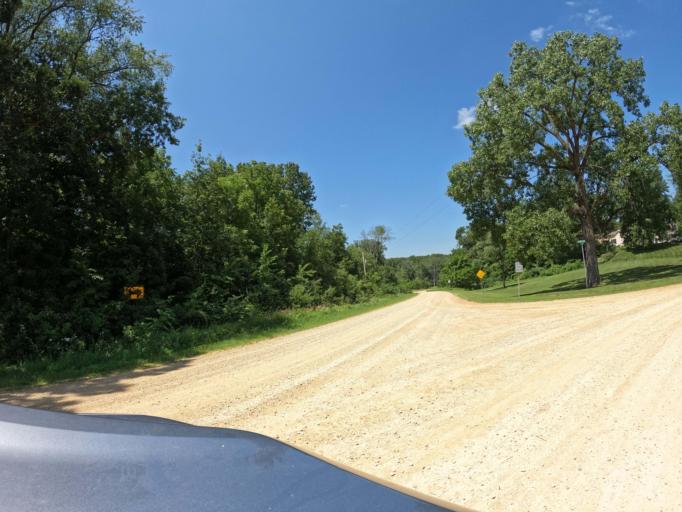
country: US
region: Iowa
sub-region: Clinton County
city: De Witt
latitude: 41.7594
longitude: -90.4323
